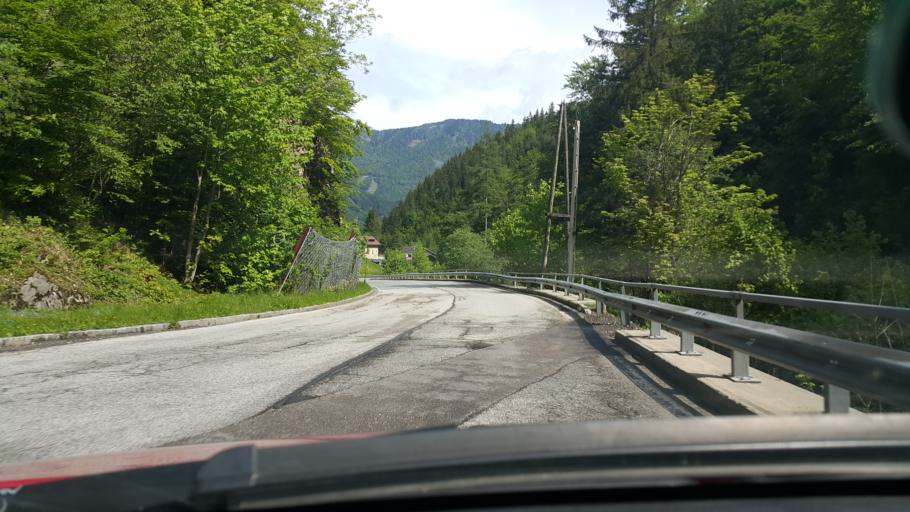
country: AT
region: Carinthia
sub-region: Politischer Bezirk Klagenfurt Land
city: Ferlach
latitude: 46.4581
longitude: 14.2591
